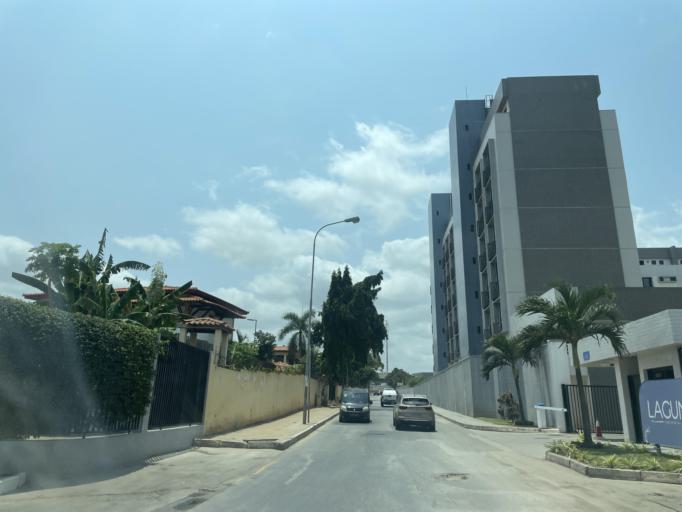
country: AO
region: Luanda
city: Luanda
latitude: -8.9091
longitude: 13.1957
